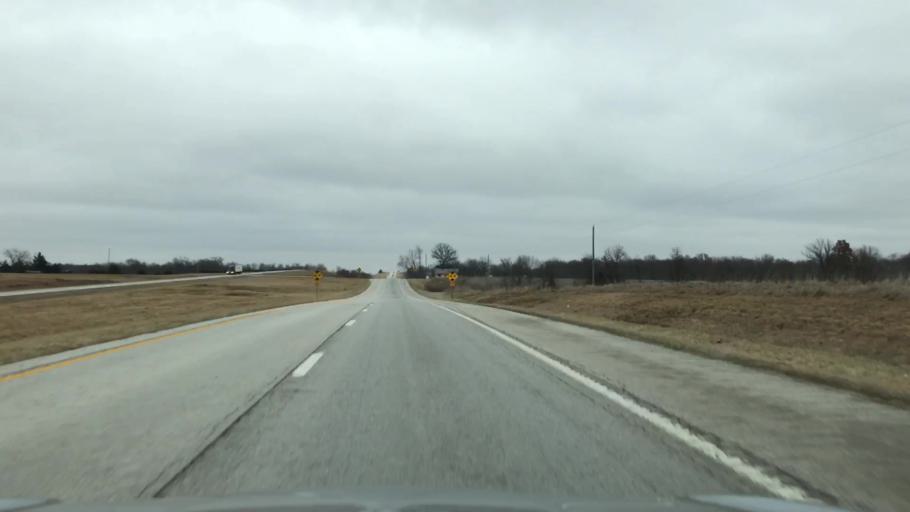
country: US
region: Missouri
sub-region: Linn County
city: Marceline
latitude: 39.7600
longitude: -92.9176
